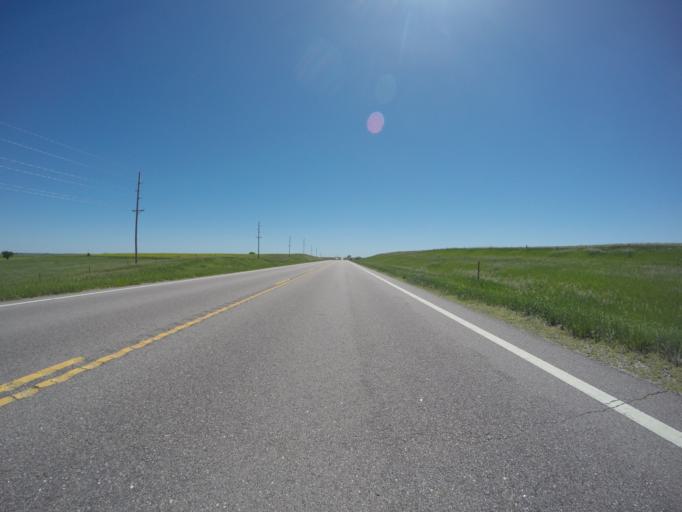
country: US
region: Kansas
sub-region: Norton County
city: Norton
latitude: 39.8284
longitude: -99.6758
